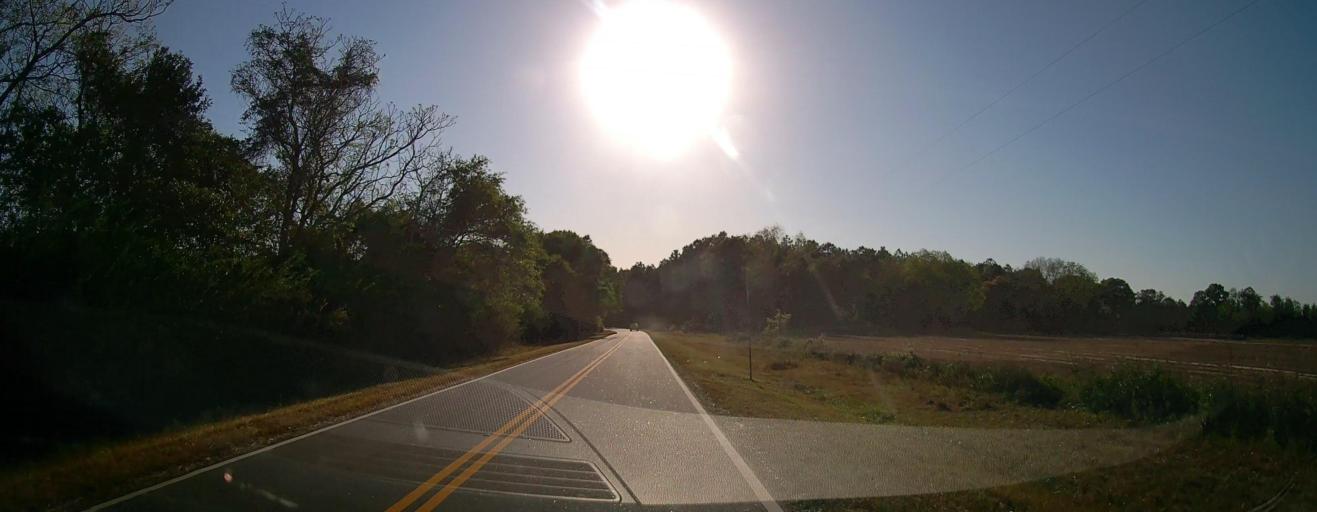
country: US
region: Georgia
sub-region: Ben Hill County
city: Fitzgerald
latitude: 31.6587
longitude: -83.1544
